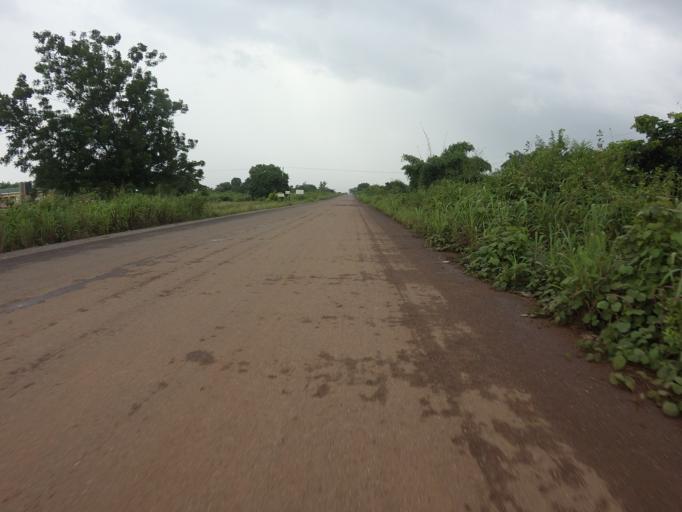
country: GH
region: Volta
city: Kpandu
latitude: 7.0219
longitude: 0.4280
